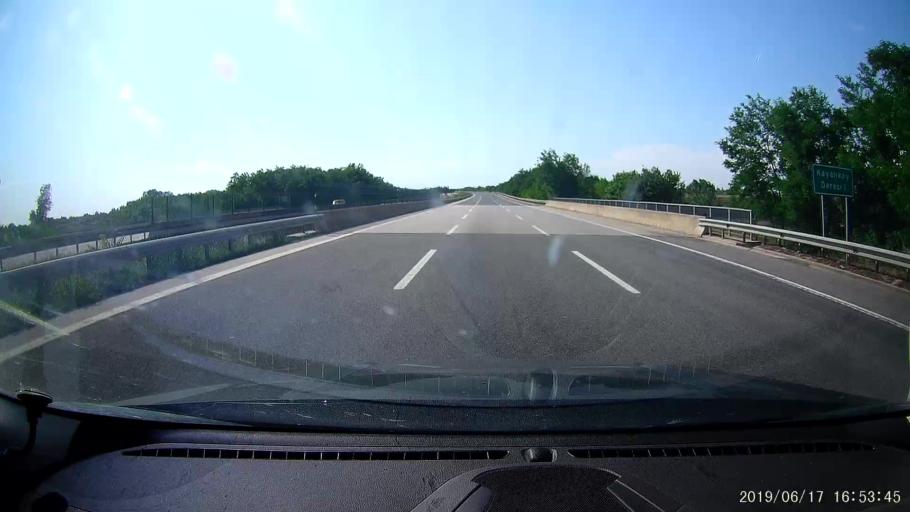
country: TR
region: Kirklareli
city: Inece
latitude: 41.5675
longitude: 27.0152
